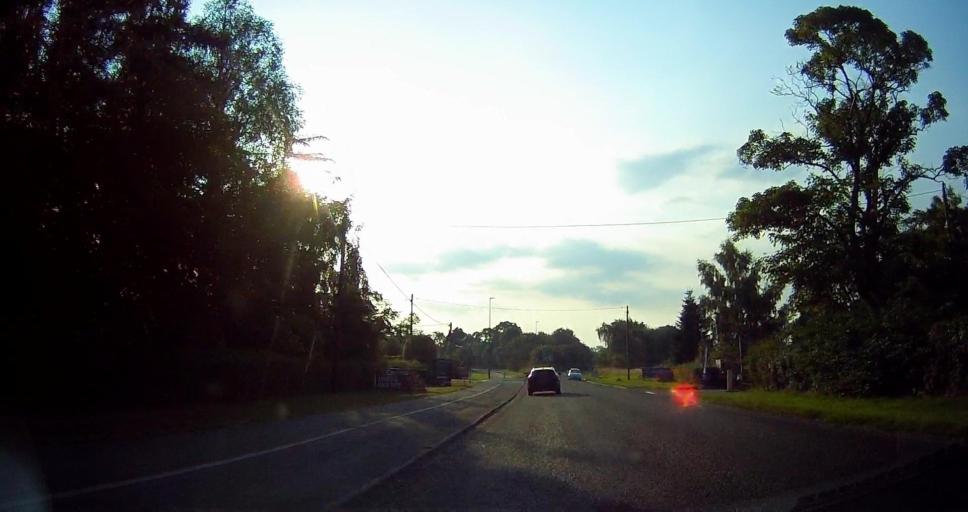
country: GB
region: England
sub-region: Cheshire East
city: Willaston
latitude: 53.0630
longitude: -2.4935
